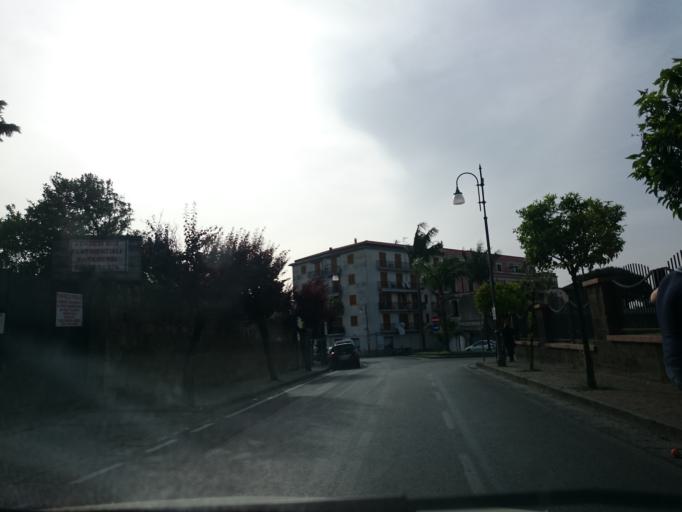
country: IT
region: Campania
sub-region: Provincia di Napoli
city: Sant'Agnello
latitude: 40.6314
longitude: 14.4060
